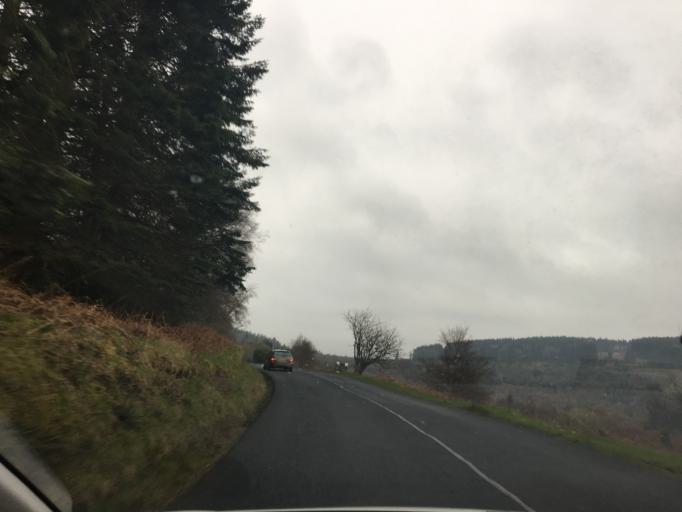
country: GB
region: Scotland
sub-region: North Ayrshire
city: Lamlash
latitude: 55.5458
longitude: -5.1337
